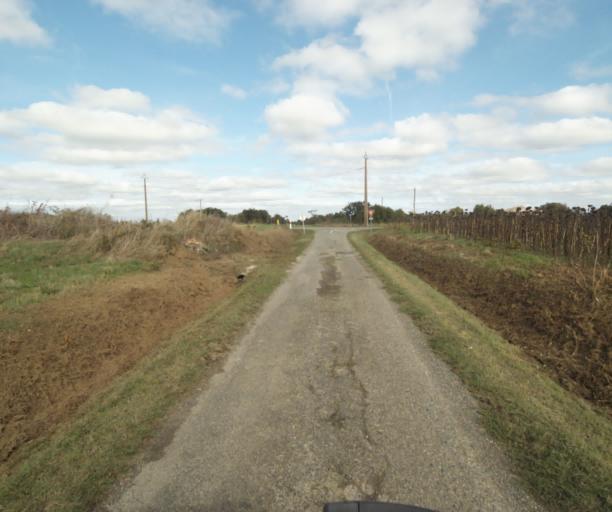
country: FR
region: Midi-Pyrenees
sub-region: Departement du Tarn-et-Garonne
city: Saint-Porquier
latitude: 43.9620
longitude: 1.1591
